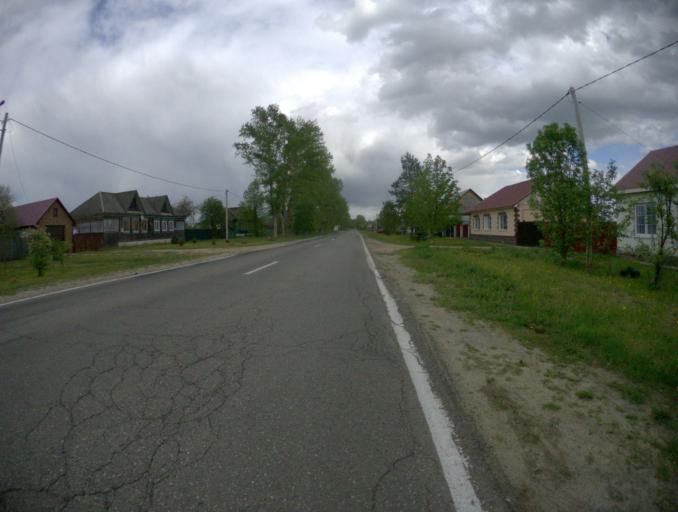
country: RU
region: Vladimir
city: Gusevskiy
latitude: 55.5740
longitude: 40.4919
